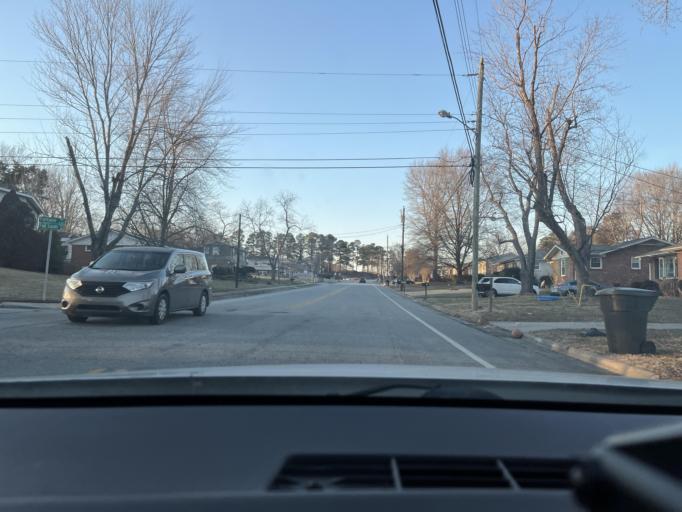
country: US
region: North Carolina
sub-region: Guilford County
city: Greensboro
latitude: 36.0359
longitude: -79.8339
